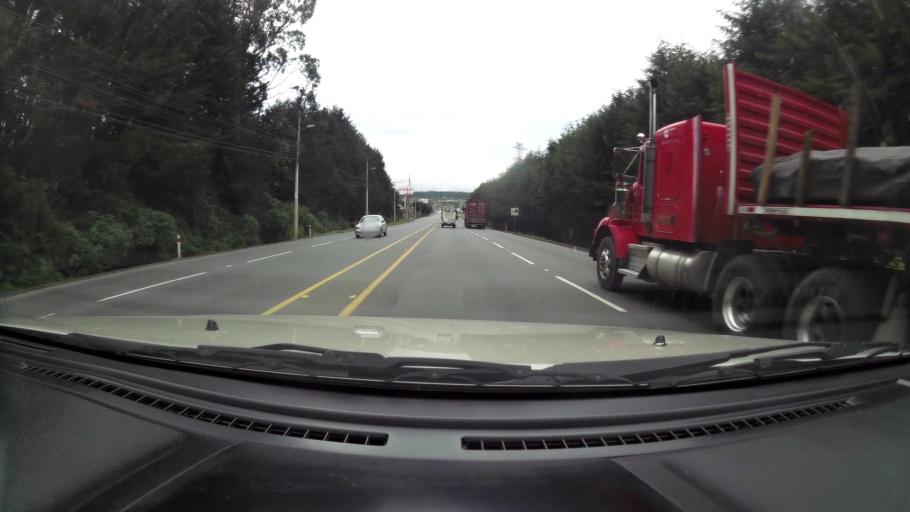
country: EC
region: Pichincha
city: Machachi
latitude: -0.4438
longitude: -78.6049
